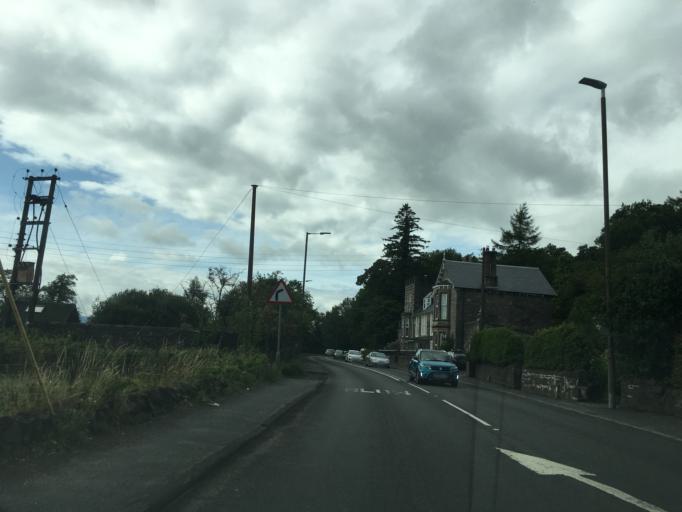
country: GB
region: Scotland
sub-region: Stirling
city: Stirling
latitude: 56.1337
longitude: -3.9082
